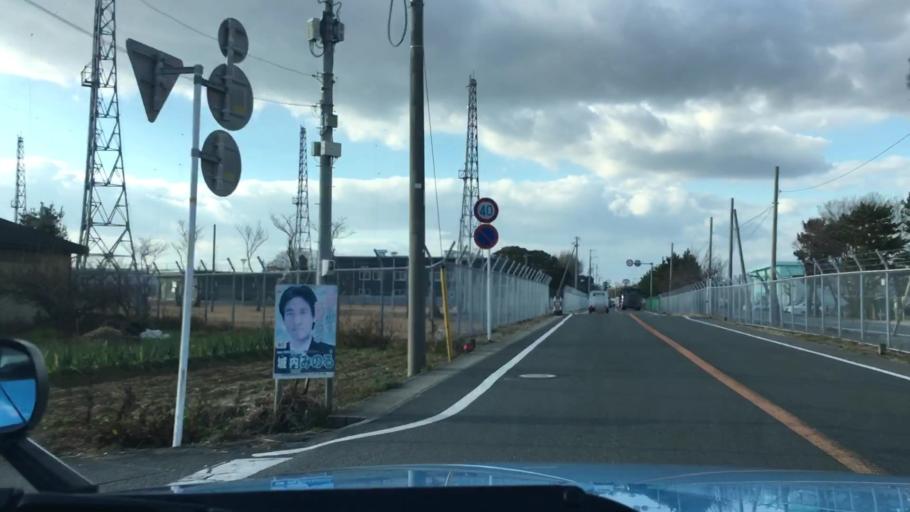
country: JP
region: Shizuoka
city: Hamamatsu
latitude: 34.7454
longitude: 137.6883
